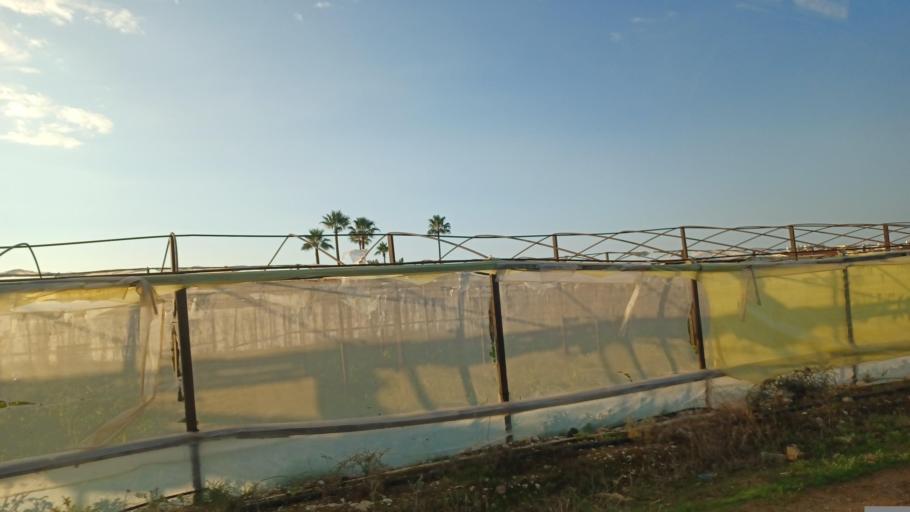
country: CY
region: Pafos
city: Kissonerga
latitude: 34.8217
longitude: 32.4119
